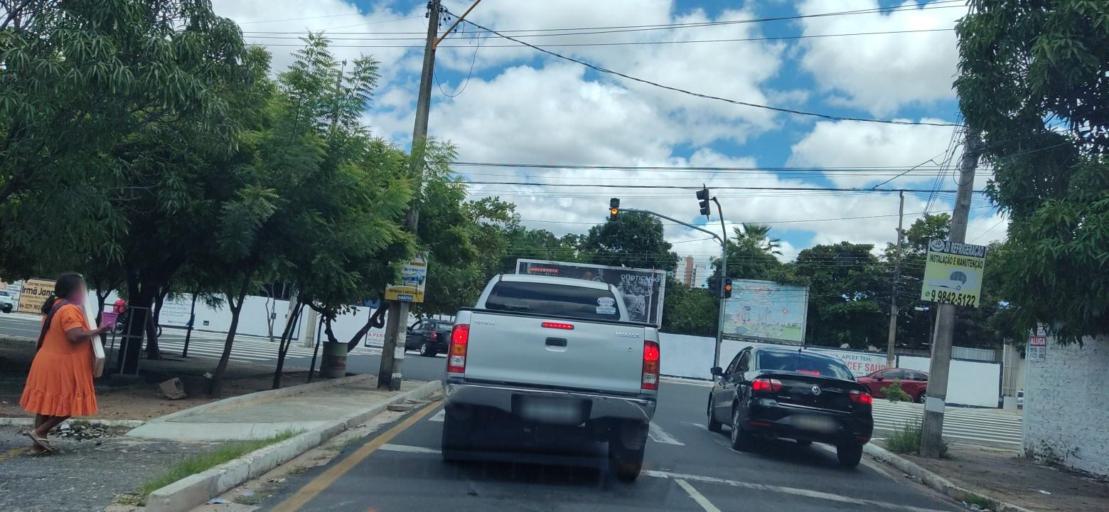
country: BR
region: Piaui
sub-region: Teresina
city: Teresina
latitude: -5.0648
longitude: -42.7697
